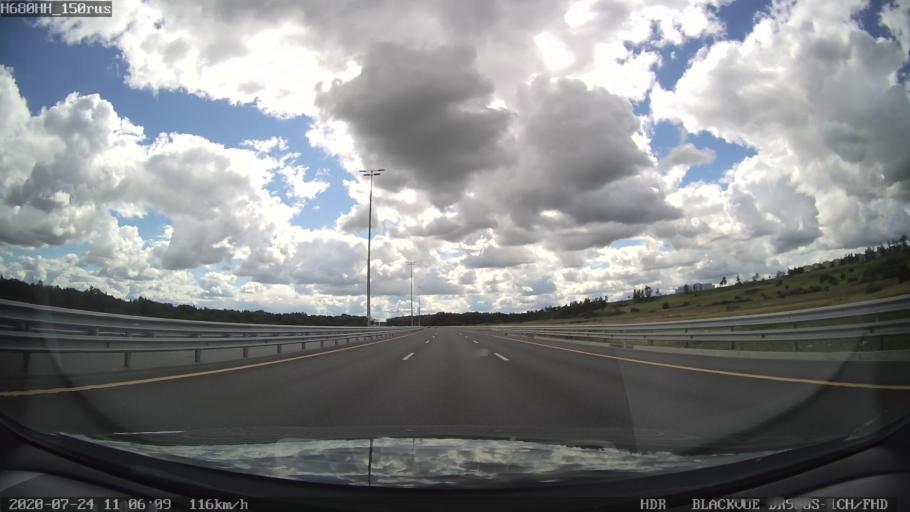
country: RU
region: St.-Petersburg
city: Shushary
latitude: 59.7673
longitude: 30.3681
